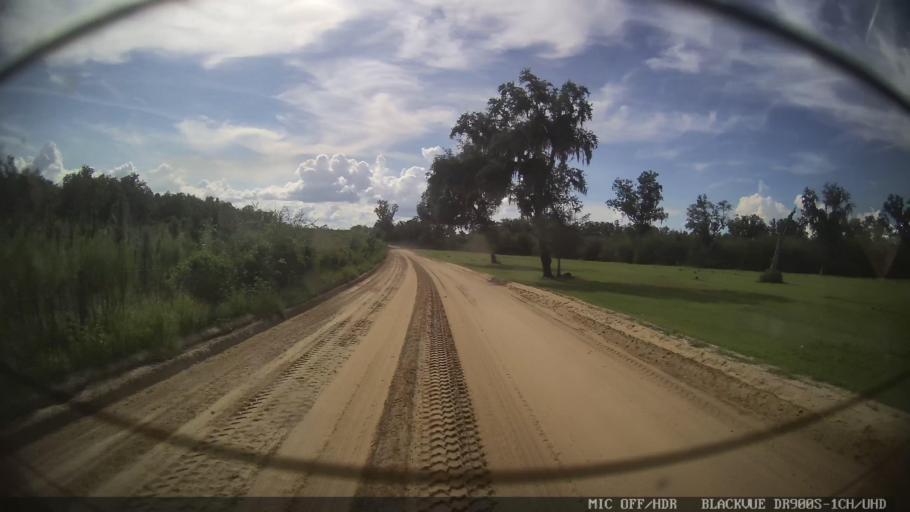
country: US
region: Georgia
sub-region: Echols County
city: Statenville
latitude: 30.6239
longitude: -83.1885
